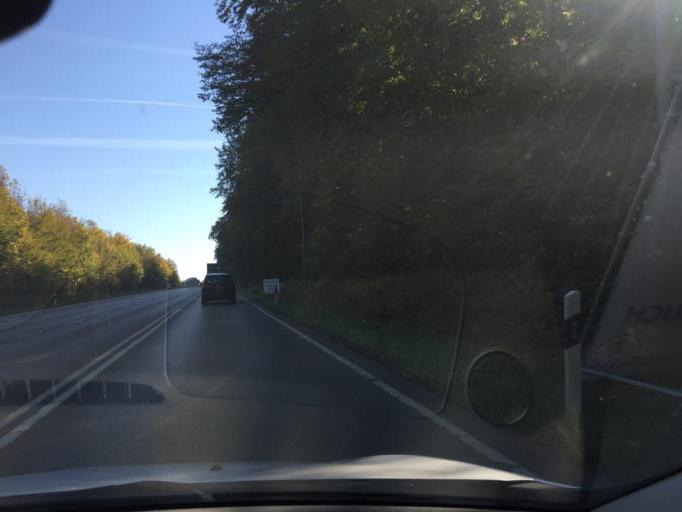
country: LU
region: Luxembourg
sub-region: Canton de Luxembourg
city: Sandweiler
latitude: 49.6145
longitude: 6.1910
